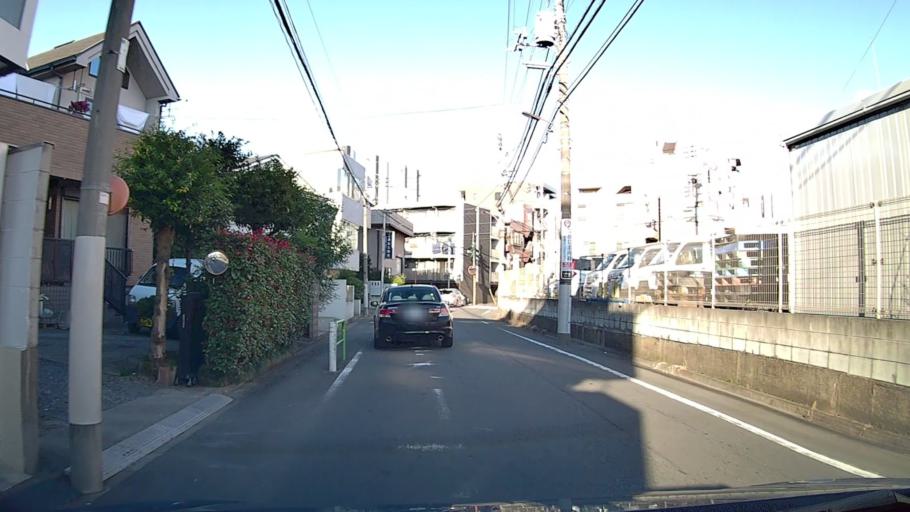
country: JP
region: Saitama
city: Wako
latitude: 35.7572
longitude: 139.5874
